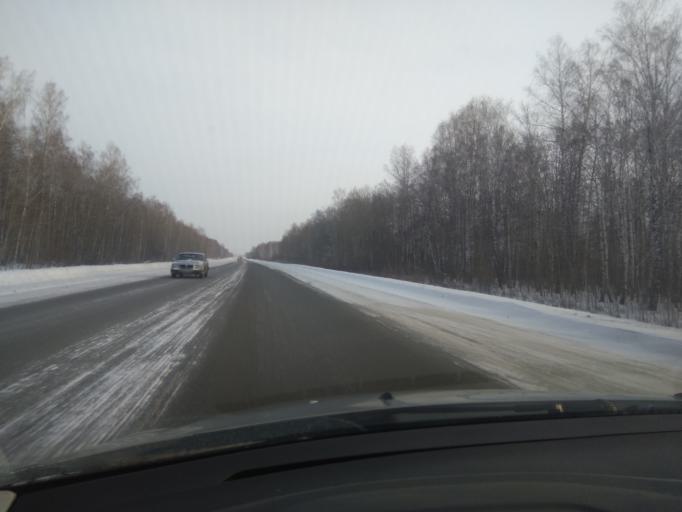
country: RU
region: Sverdlovsk
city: Bogdanovich
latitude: 56.8019
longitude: 62.0209
